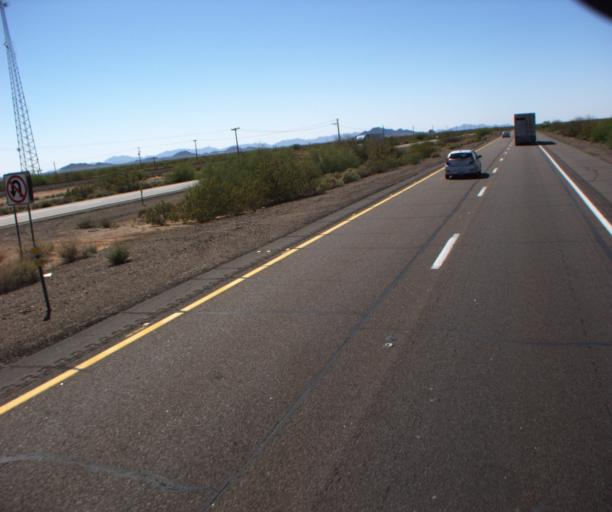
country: US
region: Arizona
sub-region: Maricopa County
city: Gila Bend
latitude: 32.8345
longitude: -113.3668
